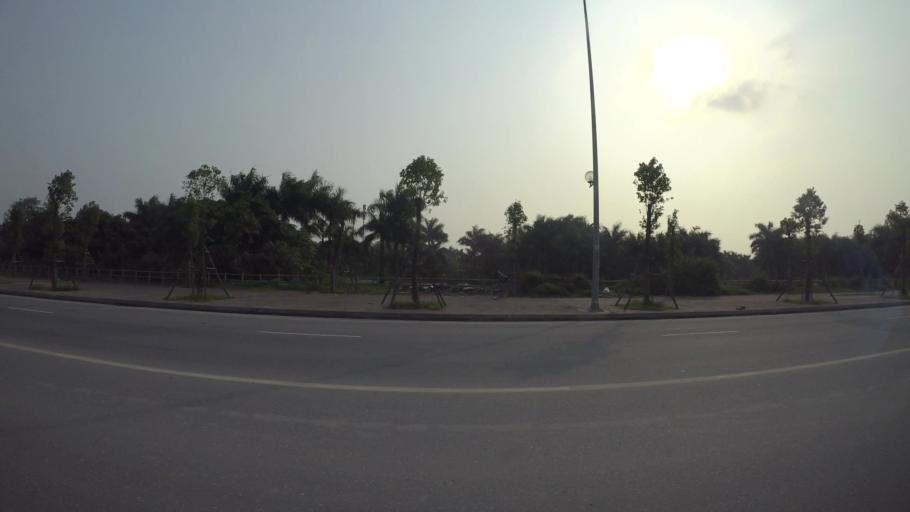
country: VN
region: Ha Noi
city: Dong Anh
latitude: 21.1165
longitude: 105.8264
